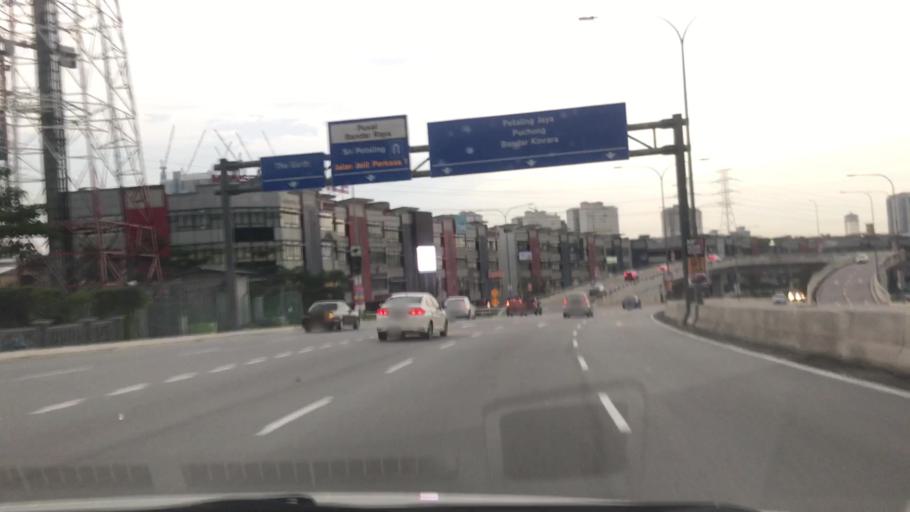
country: MY
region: Selangor
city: Kampong Baharu Balakong
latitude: 3.0486
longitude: 101.6725
